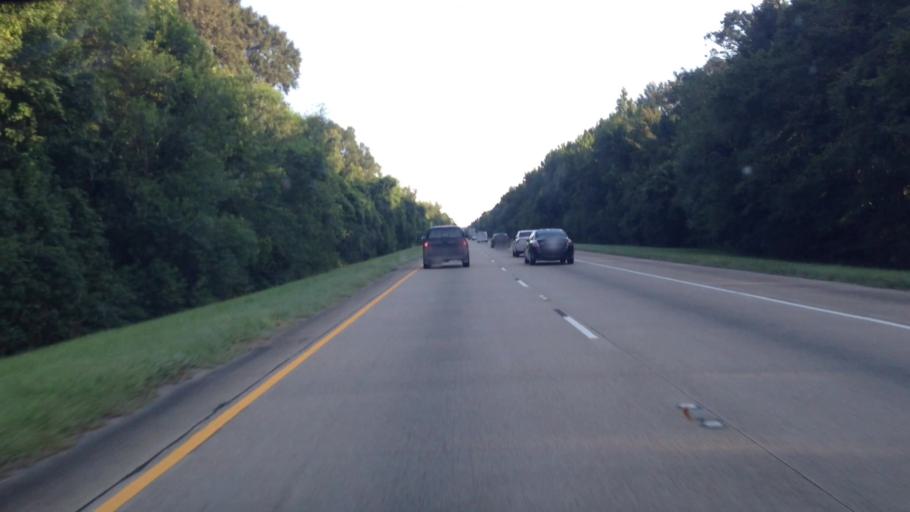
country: US
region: Louisiana
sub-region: Ascension Parish
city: Prairieville
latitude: 30.2875
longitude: -90.9899
